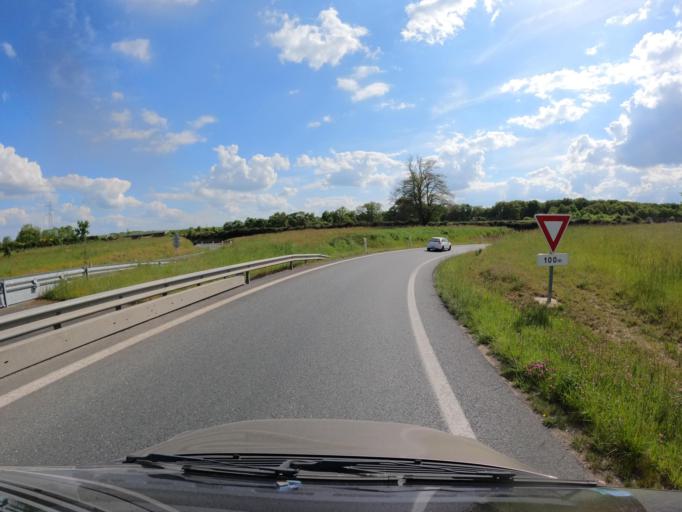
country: FR
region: Pays de la Loire
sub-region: Departement de Maine-et-Loire
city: La Tessoualle
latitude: 47.0242
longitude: -0.8825
